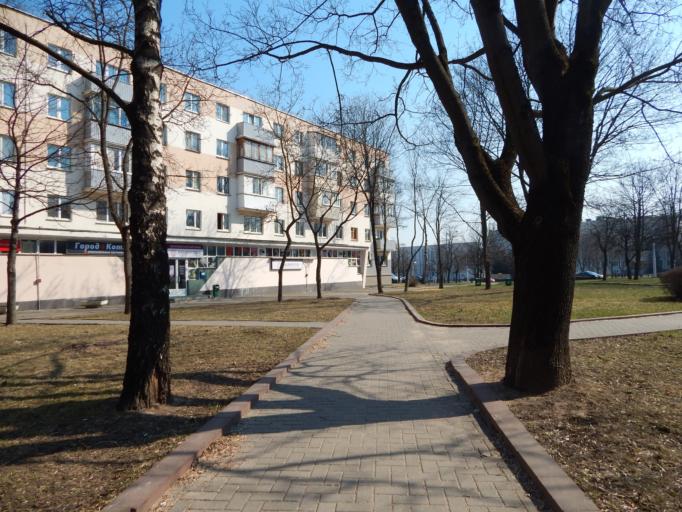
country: BY
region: Minsk
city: Minsk
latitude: 53.9100
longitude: 27.5086
